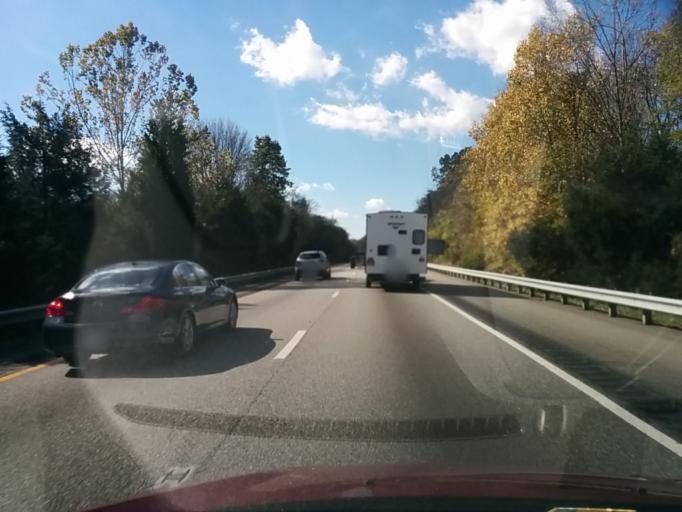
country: US
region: Virginia
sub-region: Botetourt County
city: Daleville
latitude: 37.4387
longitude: -79.8684
